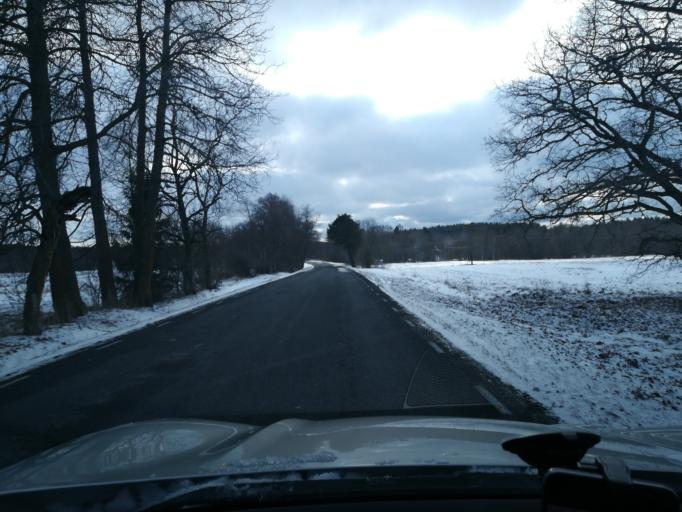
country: EE
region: Harju
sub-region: Keila linn
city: Keila
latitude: 59.4142
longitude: 24.4139
